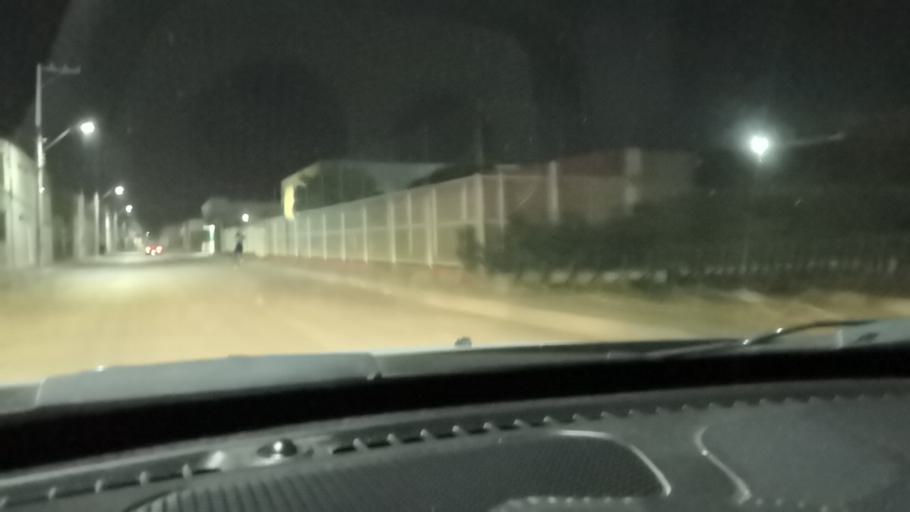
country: MX
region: Guanajuato
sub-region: Leon
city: Fraccionamiento Paraiso Real
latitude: 21.0855
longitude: -101.6236
